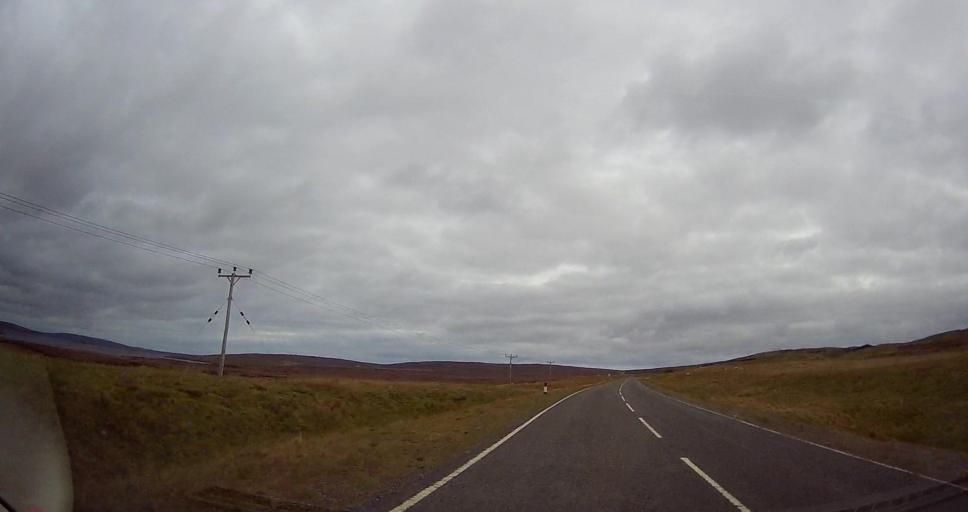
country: GB
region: Scotland
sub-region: Shetland Islands
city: Shetland
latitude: 60.6519
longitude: -1.0667
